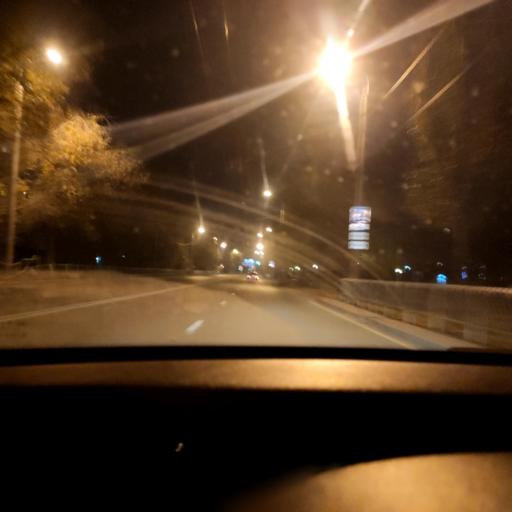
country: RU
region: Samara
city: Samara
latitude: 53.2411
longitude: 50.2277
